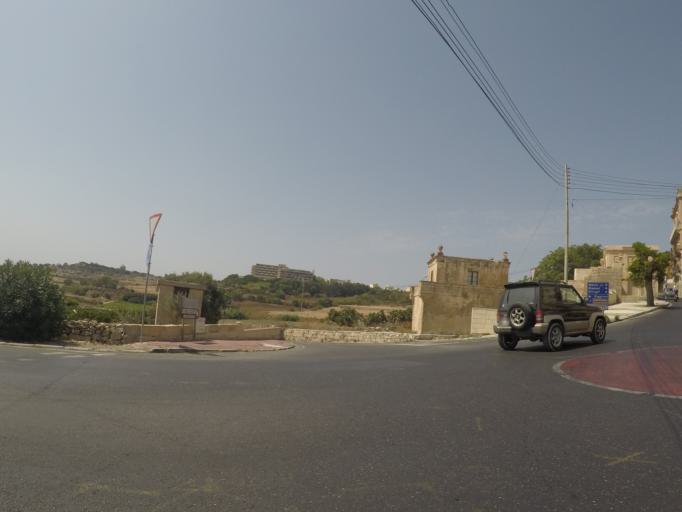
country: MT
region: L-Imdina
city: Imdina
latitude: 35.8836
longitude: 14.4052
